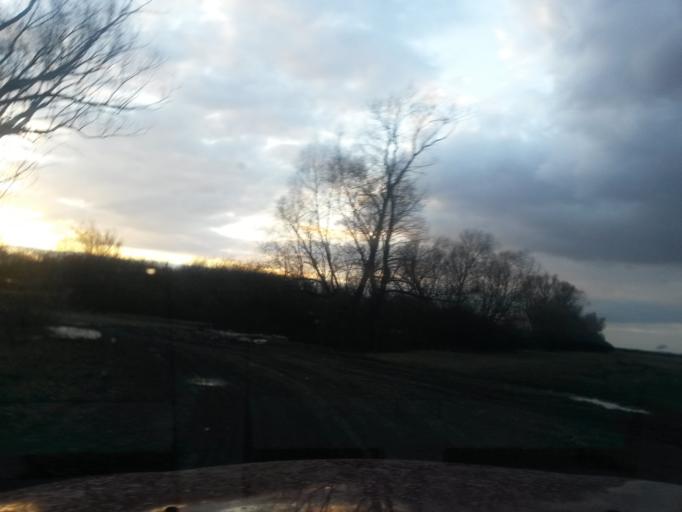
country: SK
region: Kosicky
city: Sobrance
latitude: 48.7030
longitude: 22.0667
